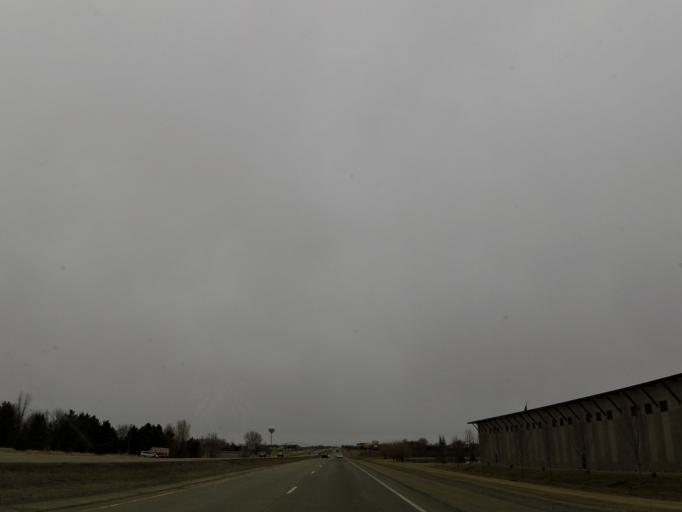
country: US
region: Minnesota
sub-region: Le Sueur County
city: Le Sueur
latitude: 44.4929
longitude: -93.8731
